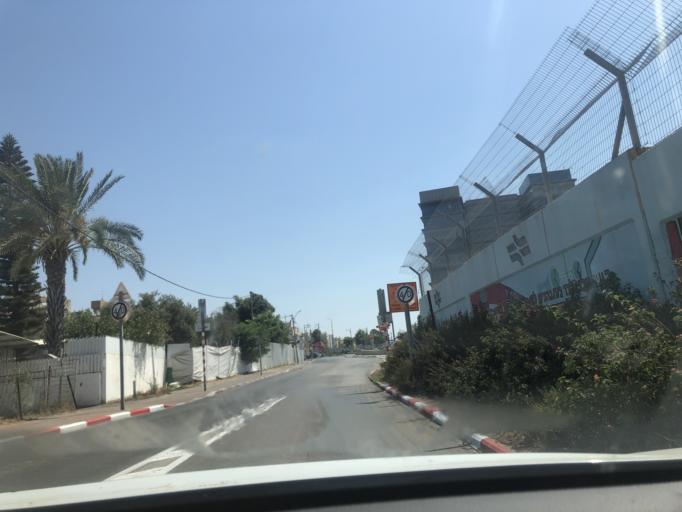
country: IL
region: Central District
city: Lod
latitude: 31.9492
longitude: 34.8815
